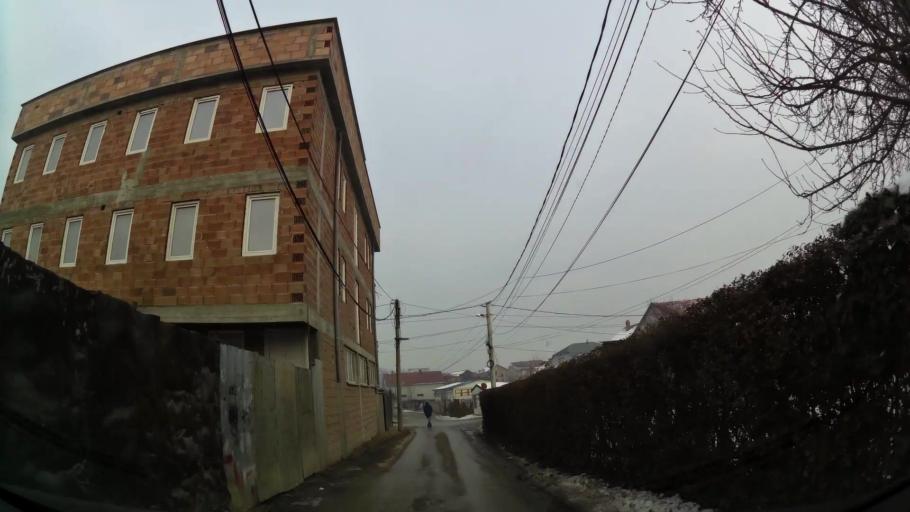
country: MK
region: Suto Orizari
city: Suto Orizare
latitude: 42.0332
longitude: 21.4227
